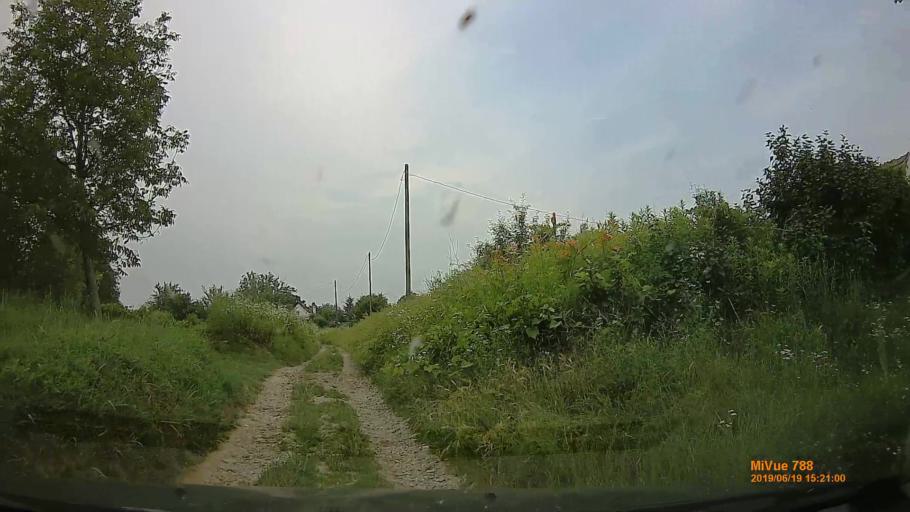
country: HU
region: Baranya
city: Szigetvar
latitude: 46.0701
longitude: 17.8479
